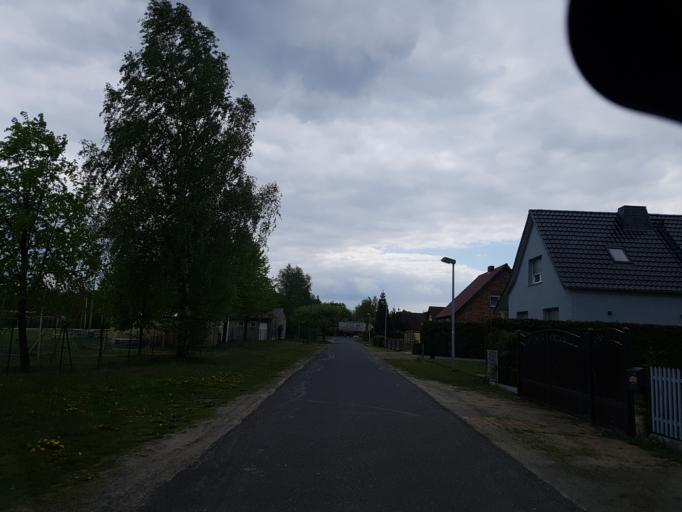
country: DE
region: Brandenburg
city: Sallgast
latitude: 51.6024
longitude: 13.9083
